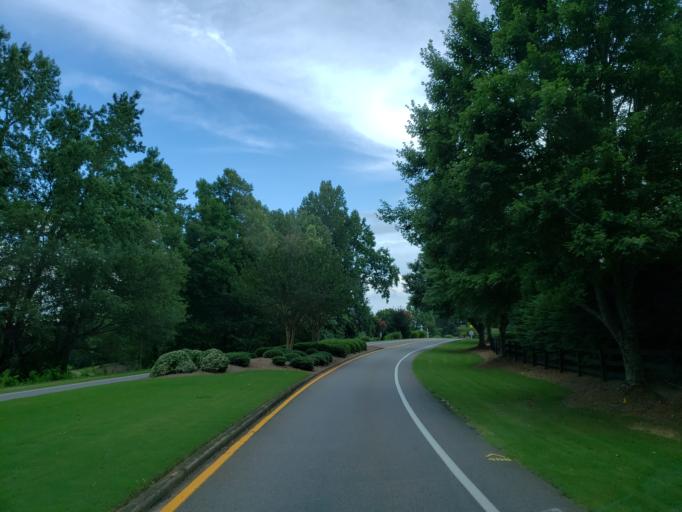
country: US
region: Georgia
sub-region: Cherokee County
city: Ball Ground
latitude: 34.2338
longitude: -84.3555
